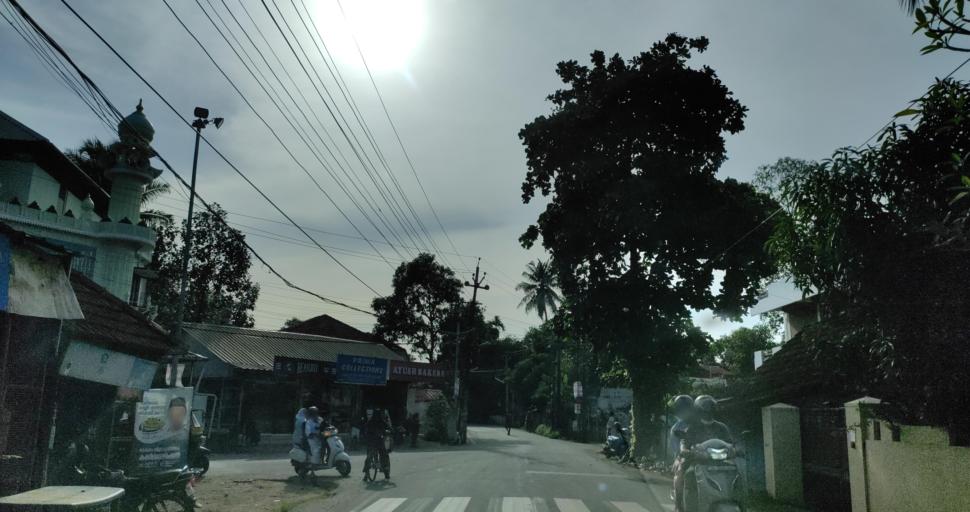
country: IN
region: Kerala
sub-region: Kottayam
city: Kottayam
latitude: 9.5851
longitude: 76.4989
